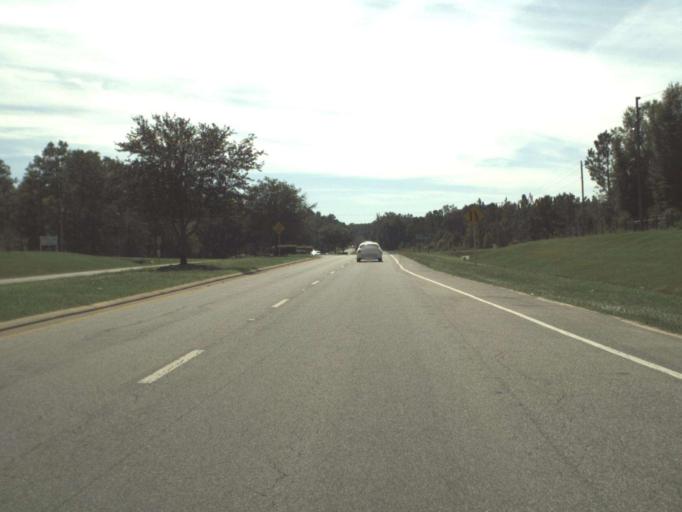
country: US
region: Florida
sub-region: Washington County
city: Chipley
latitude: 30.7458
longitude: -85.5525
